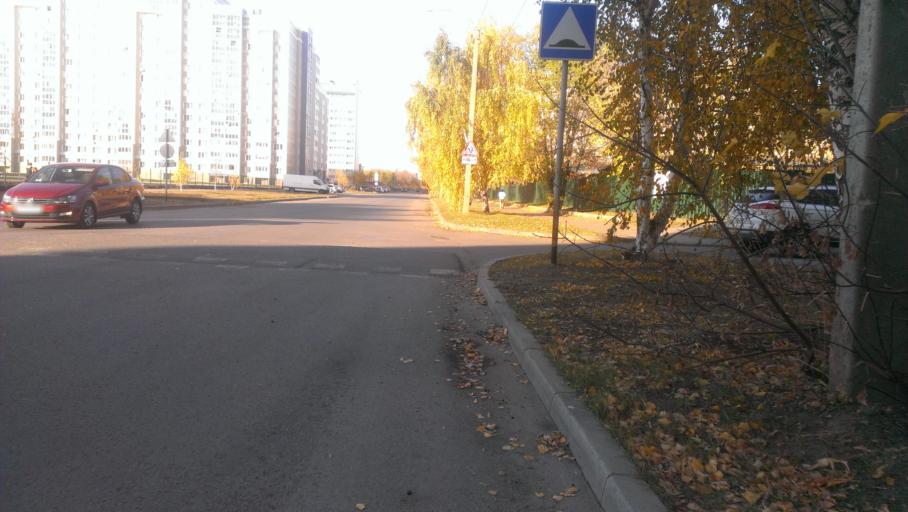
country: RU
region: Altai Krai
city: Novosilikatnyy
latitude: 53.3418
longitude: 83.6621
